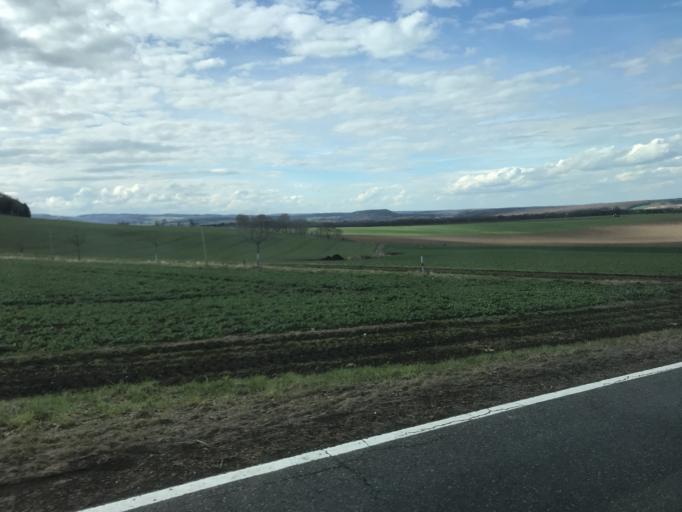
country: DE
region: Rheinland-Pfalz
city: Wassenach
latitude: 50.4318
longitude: 7.2754
